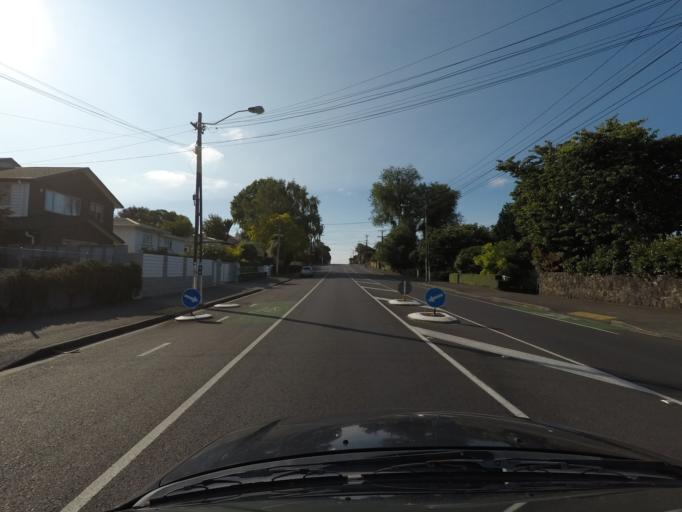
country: NZ
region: Auckland
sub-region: Auckland
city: Auckland
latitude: -36.8877
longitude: 174.7209
